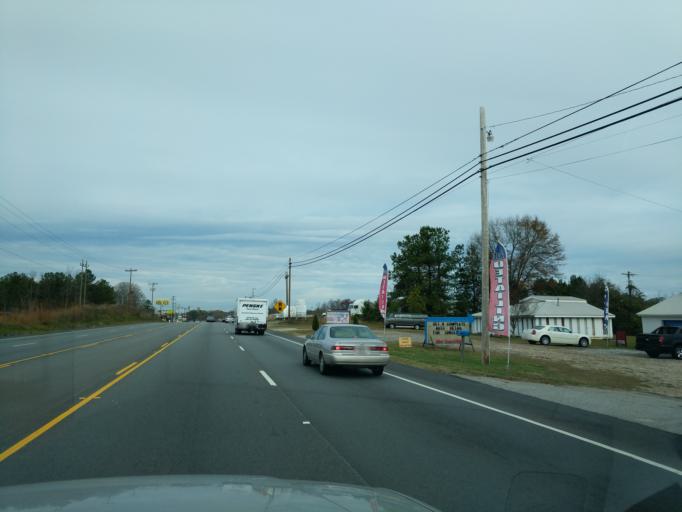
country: US
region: South Carolina
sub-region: Anderson County
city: Pendleton
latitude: 34.6273
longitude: -82.7801
